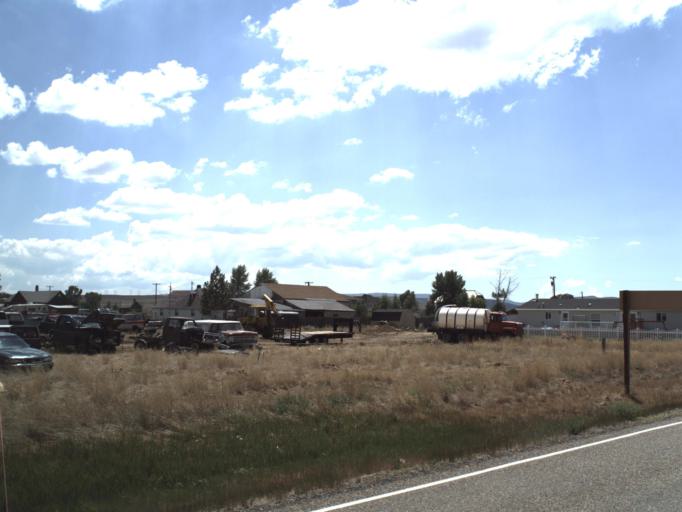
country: US
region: Utah
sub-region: Rich County
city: Randolph
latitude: 41.5241
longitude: -111.1611
